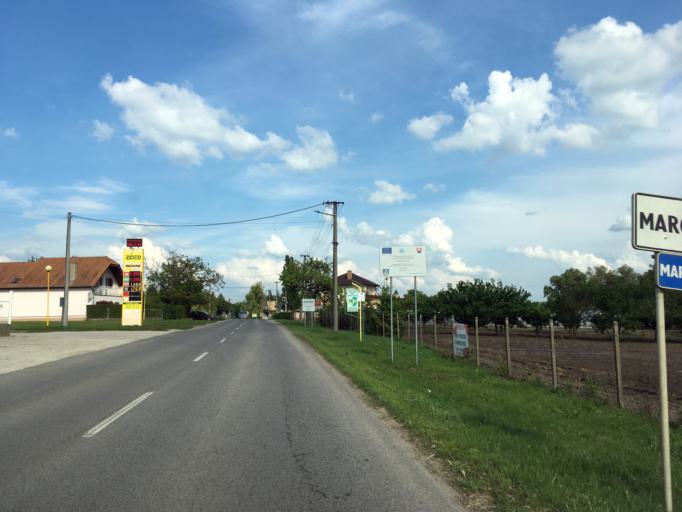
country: HU
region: Komarom-Esztergom
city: Almasfuzito
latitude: 47.7884
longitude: 18.2648
